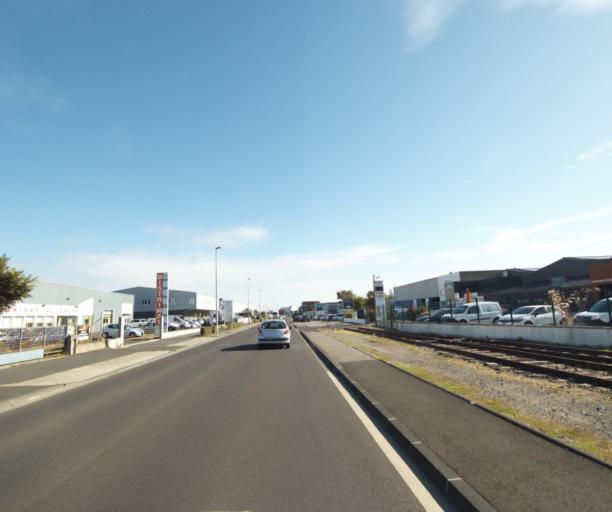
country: FR
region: Auvergne
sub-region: Departement du Puy-de-Dome
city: Aulnat
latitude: 45.7848
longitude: 3.1334
